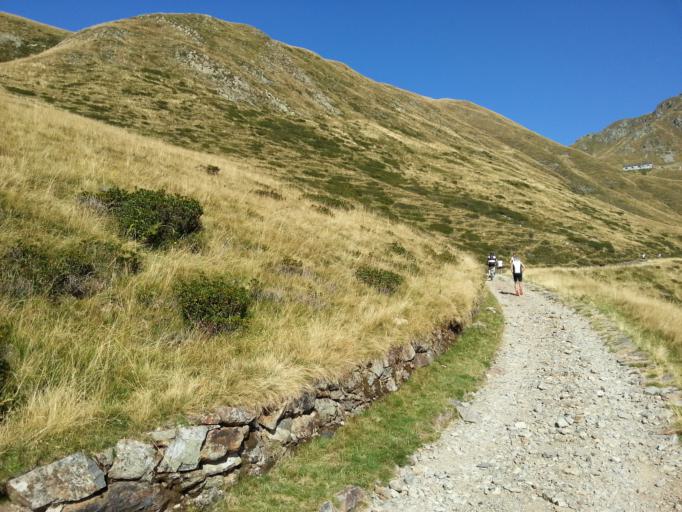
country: IT
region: Lombardy
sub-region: Provincia di Como
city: San Bartolomeo Val Cavargna
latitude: 46.1618
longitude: 9.1635
